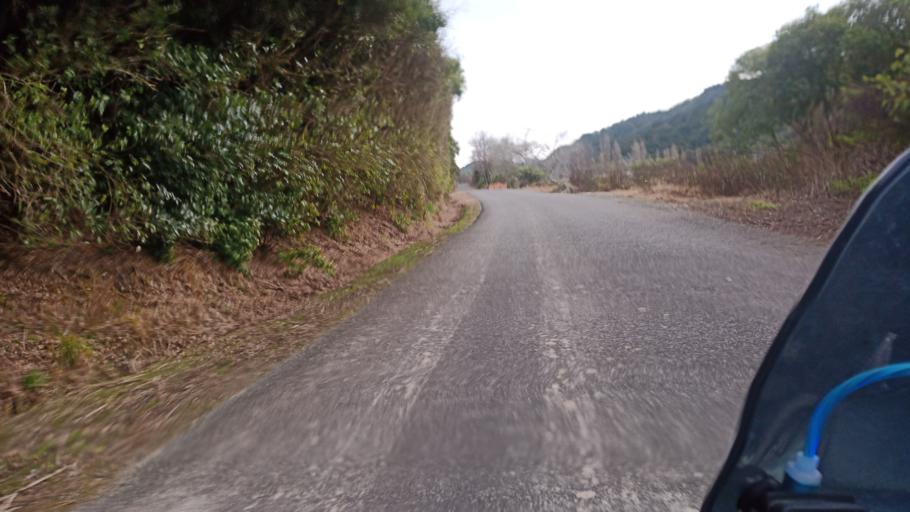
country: NZ
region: Hawke's Bay
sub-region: Wairoa District
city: Wairoa
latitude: -38.8239
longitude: 177.4995
